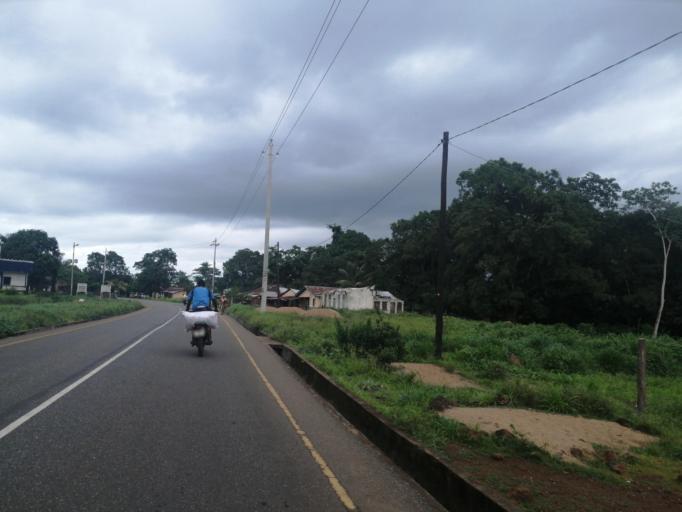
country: SL
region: Northern Province
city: Port Loko
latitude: 8.7502
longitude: -12.7820
